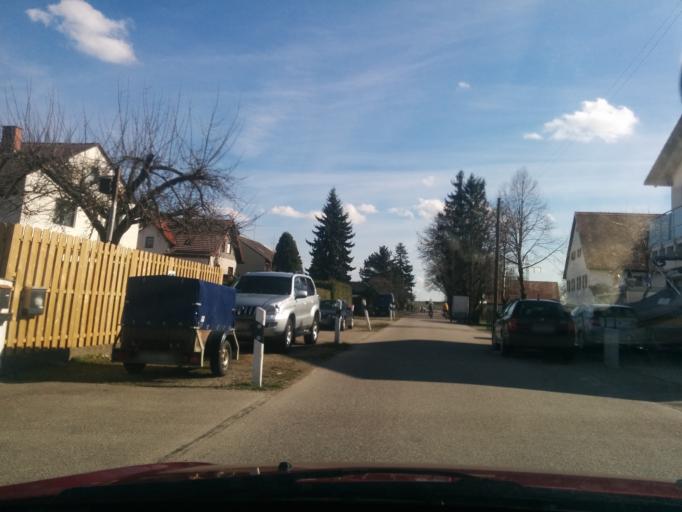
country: DE
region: Bavaria
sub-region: Upper Bavaria
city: Pasing
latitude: 48.1807
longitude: 11.4248
